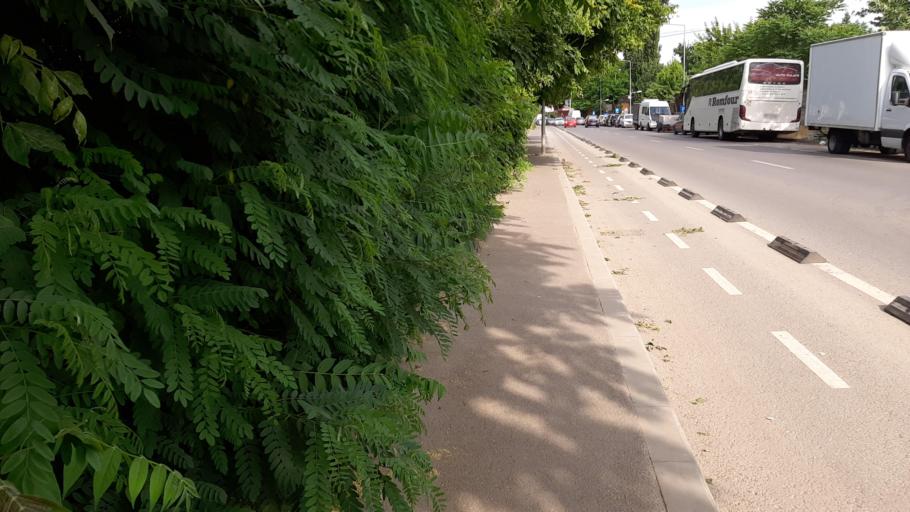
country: RO
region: Galati
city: Galati
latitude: 45.4398
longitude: 28.0307
